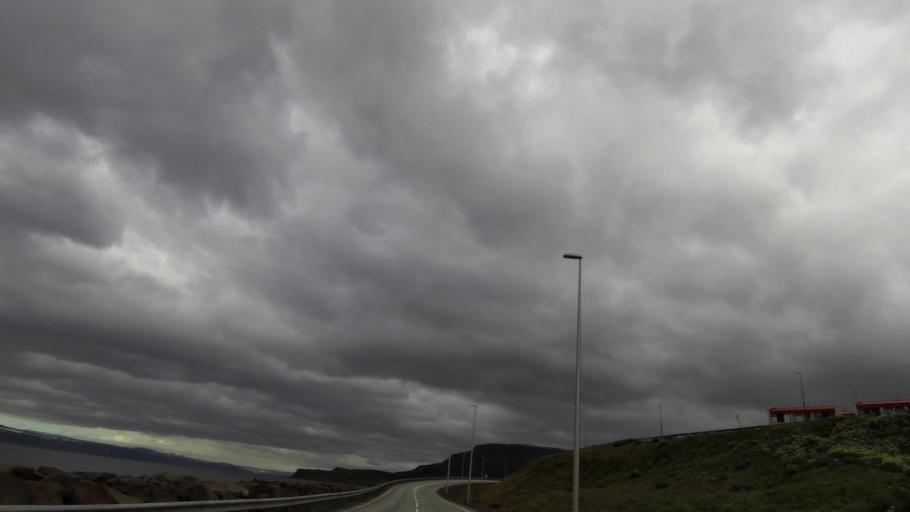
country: IS
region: Westfjords
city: Isafjoerdur
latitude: 66.1093
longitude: -23.1167
